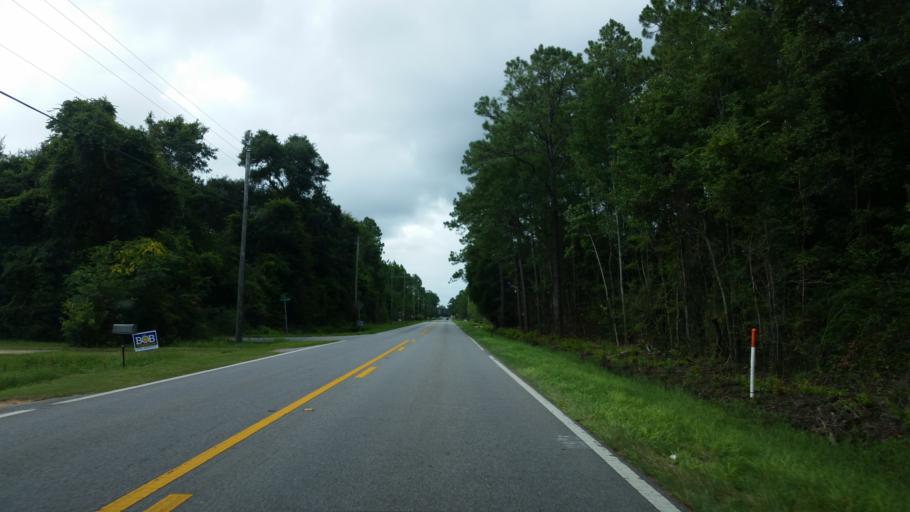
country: US
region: Florida
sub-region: Santa Rosa County
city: East Milton
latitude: 30.6132
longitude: -87.0216
